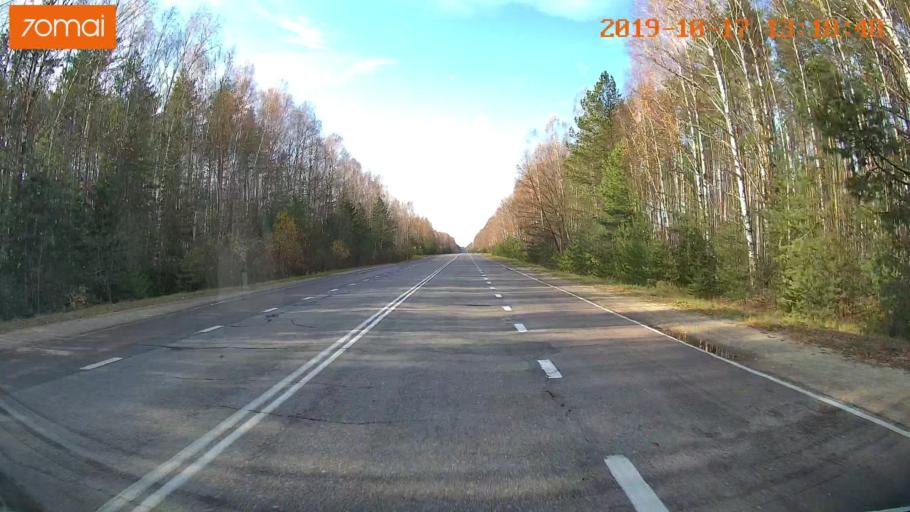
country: RU
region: Rjazan
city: Gus'-Zheleznyy
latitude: 55.0653
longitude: 41.0893
